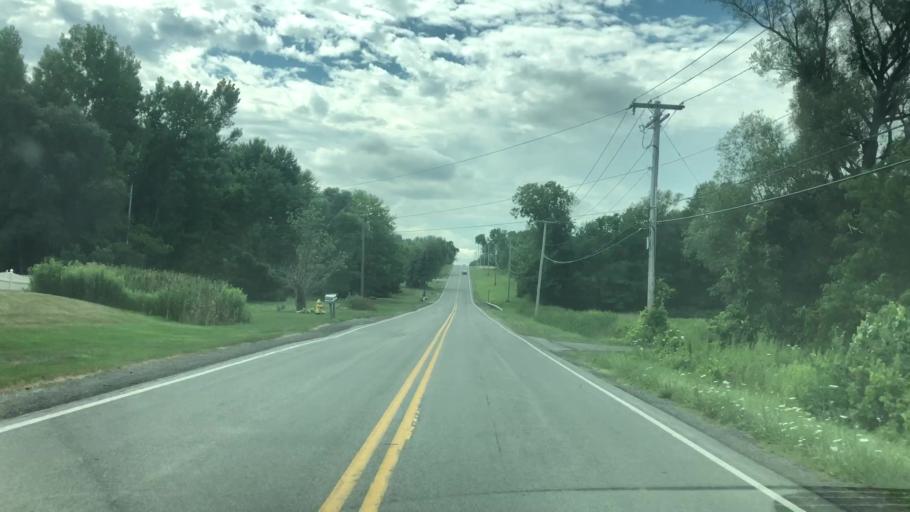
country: US
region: New York
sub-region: Monroe County
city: Fairport
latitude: 43.0733
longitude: -77.3922
